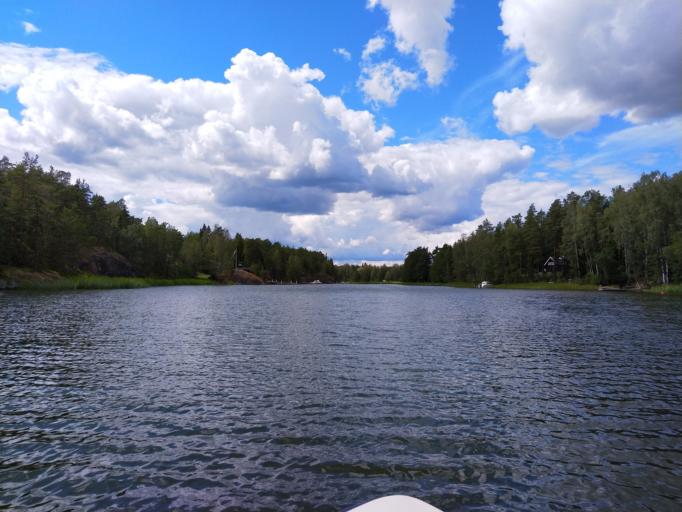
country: FI
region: Uusimaa
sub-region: Raaseporin
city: Karis
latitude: 59.9704
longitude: 23.7136
